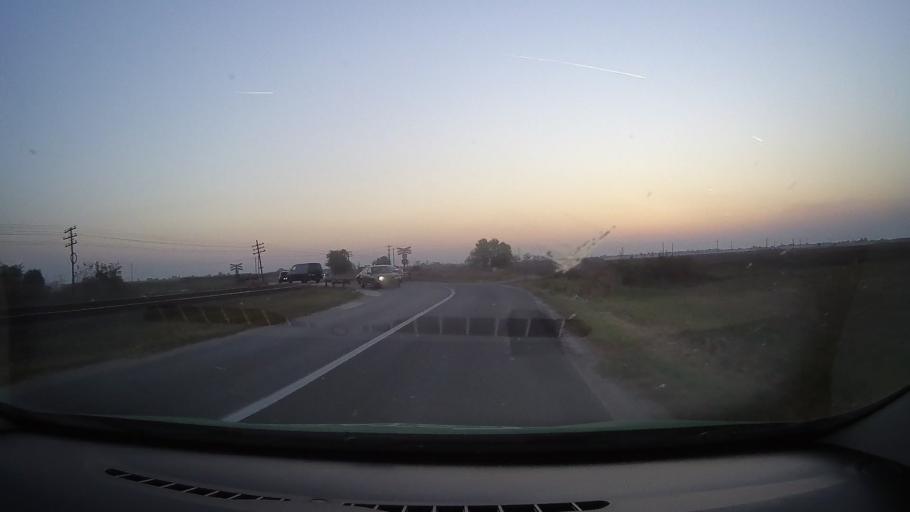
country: RO
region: Arad
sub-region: Comuna Zimandu Nou
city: Zimandu Nou
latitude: 46.2885
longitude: 21.4107
